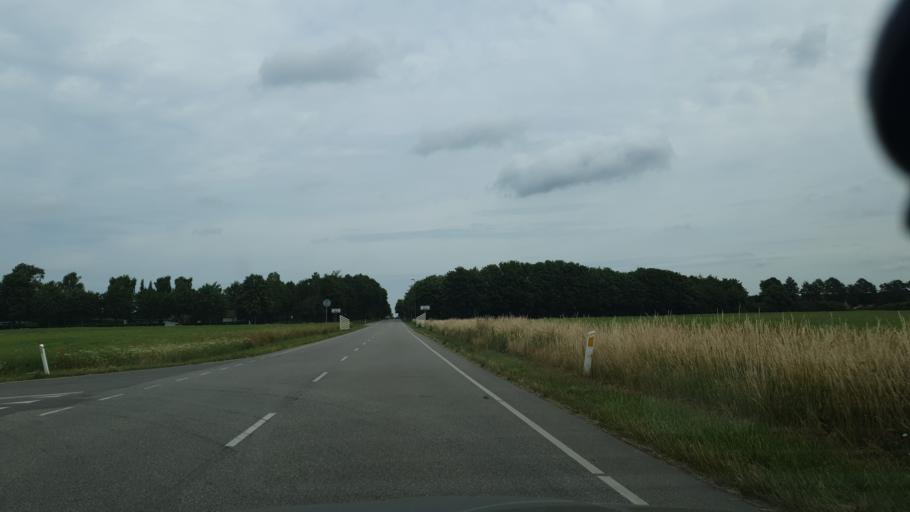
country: DK
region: Zealand
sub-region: Soro Kommune
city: Frederiksberg
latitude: 55.4051
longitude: 11.5638
